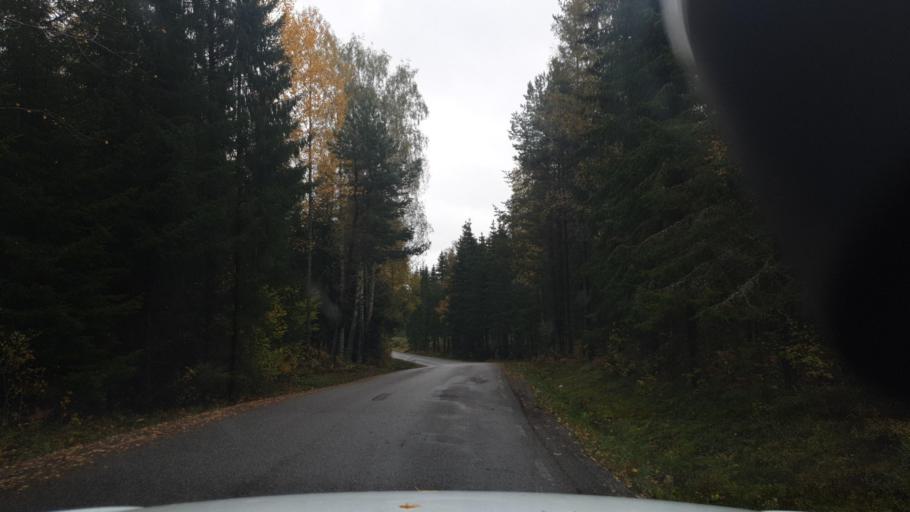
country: SE
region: Vaermland
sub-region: Karlstads Kommun
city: Valberg
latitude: 59.4143
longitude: 13.1607
